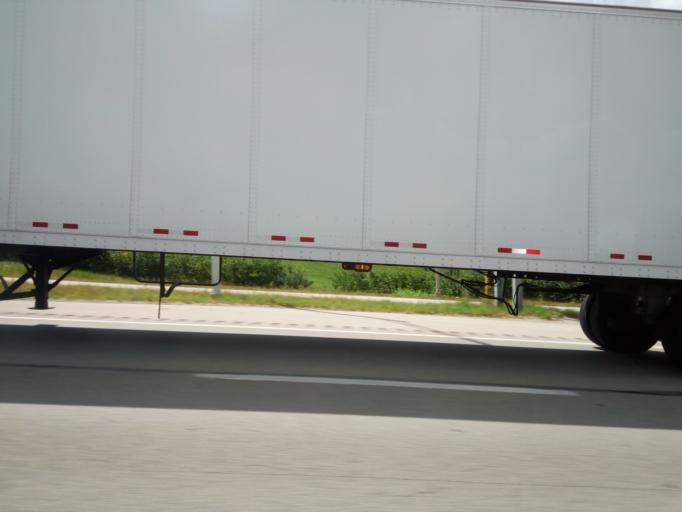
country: US
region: Kentucky
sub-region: Fayette County
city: Lexington-Fayette
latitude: 38.0250
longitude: -84.4146
